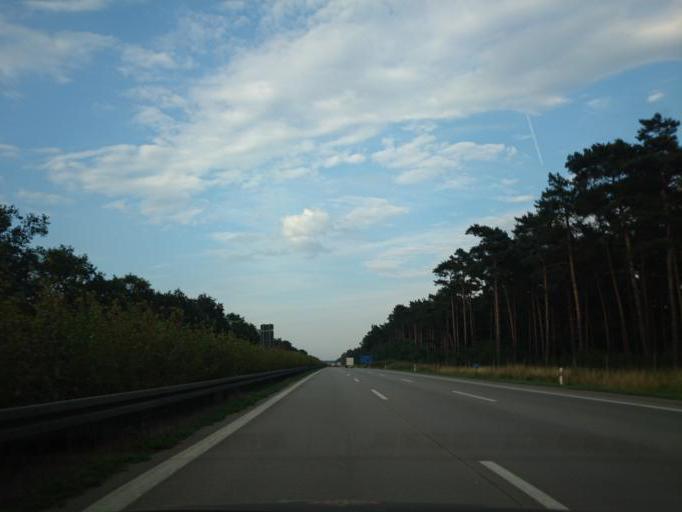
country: DE
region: Brandenburg
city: Wildau
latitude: 52.3152
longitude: 13.6743
